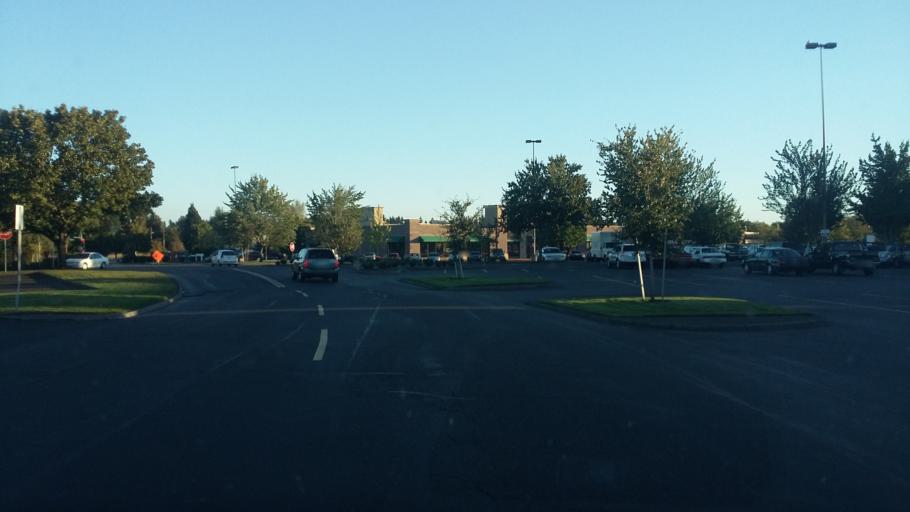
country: US
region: Washington
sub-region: Clark County
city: Walnut Grove
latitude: 45.6483
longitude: -122.5945
